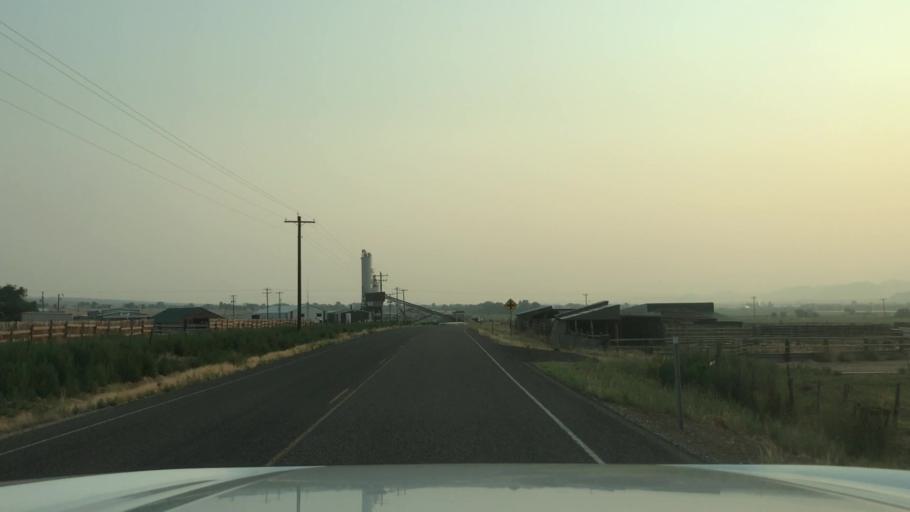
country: US
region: Utah
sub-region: Sevier County
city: Aurora
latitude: 38.9000
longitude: -111.9481
